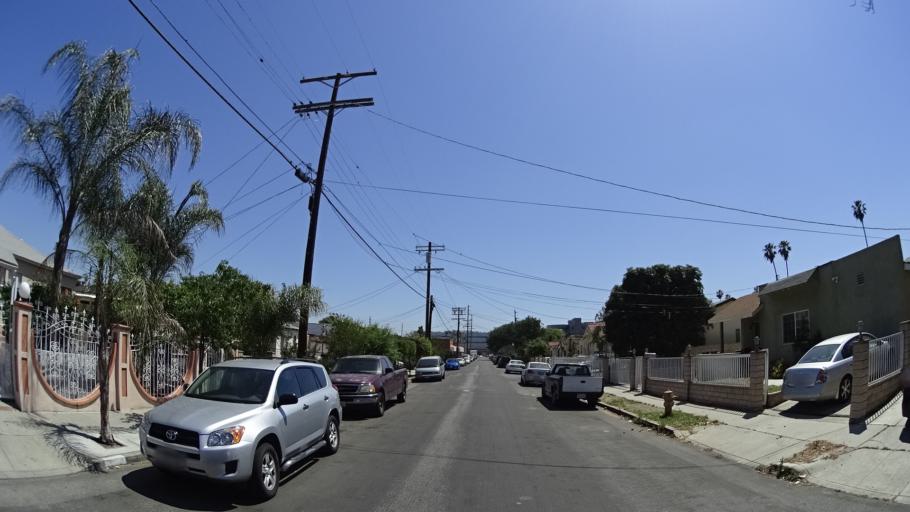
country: US
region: California
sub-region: Los Angeles County
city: North Hollywood
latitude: 34.1741
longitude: -118.3711
